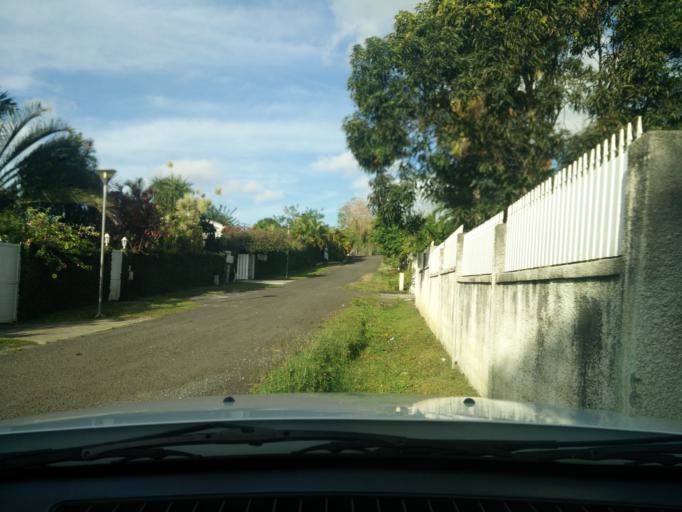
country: GP
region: Guadeloupe
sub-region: Guadeloupe
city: Baie-Mahault
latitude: 16.2571
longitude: -61.5854
